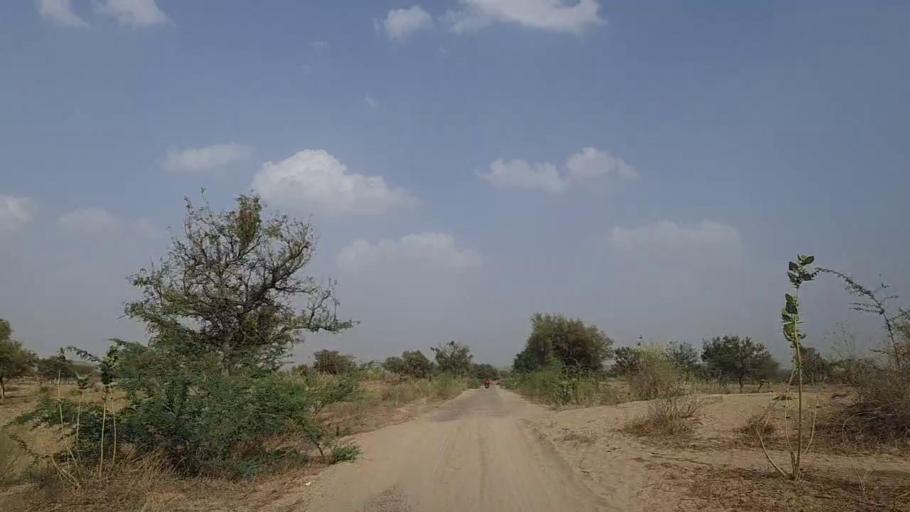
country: PK
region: Sindh
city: Islamkot
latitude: 24.8742
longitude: 70.1491
